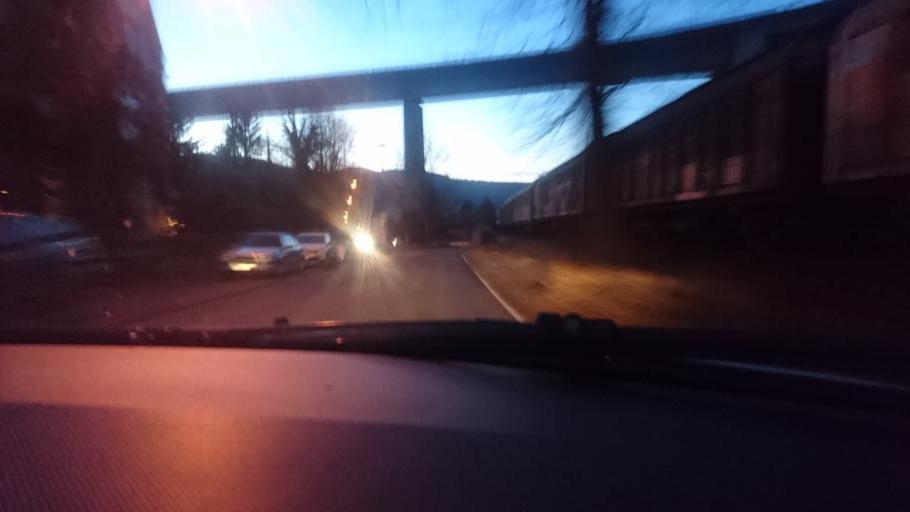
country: DE
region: Rheinland-Pfalz
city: Lahnstein
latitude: 50.3091
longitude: 7.6134
